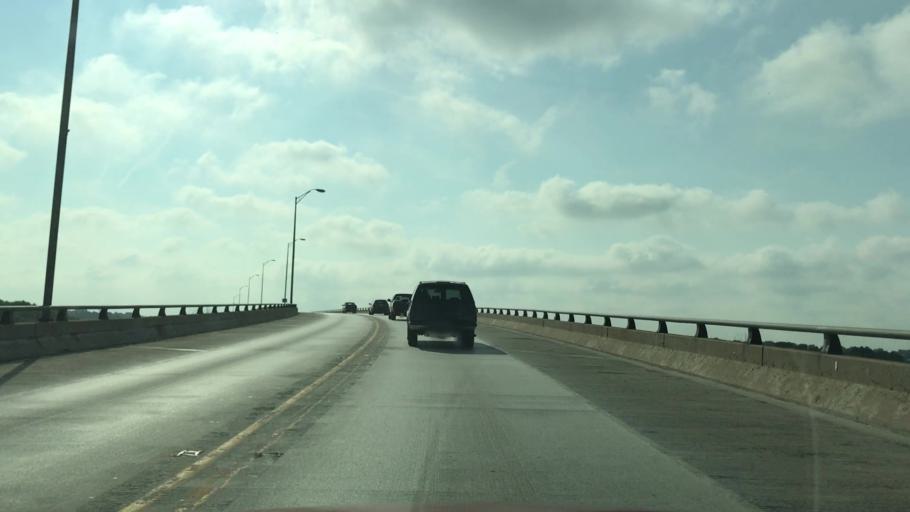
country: US
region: Illinois
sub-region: Will County
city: Lockport
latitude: 41.5917
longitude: -88.0687
